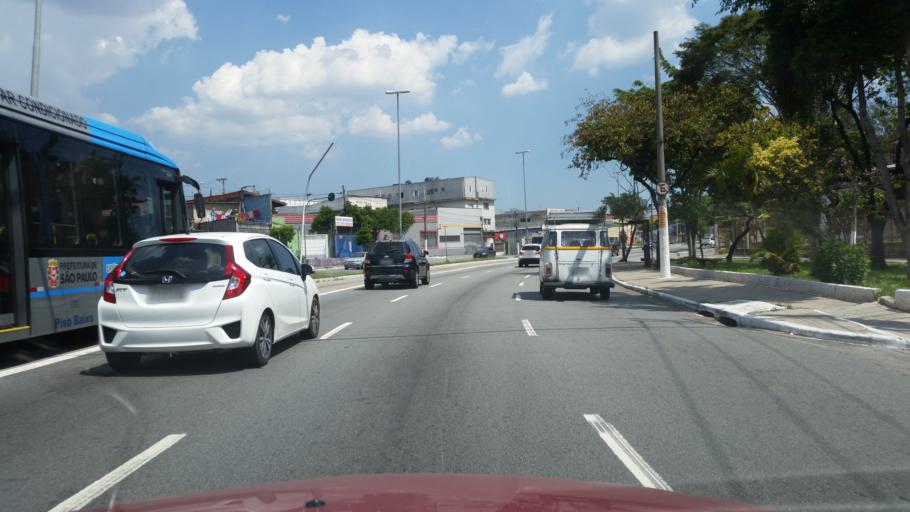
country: BR
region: Sao Paulo
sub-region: Diadema
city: Diadema
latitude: -23.6587
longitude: -46.6636
